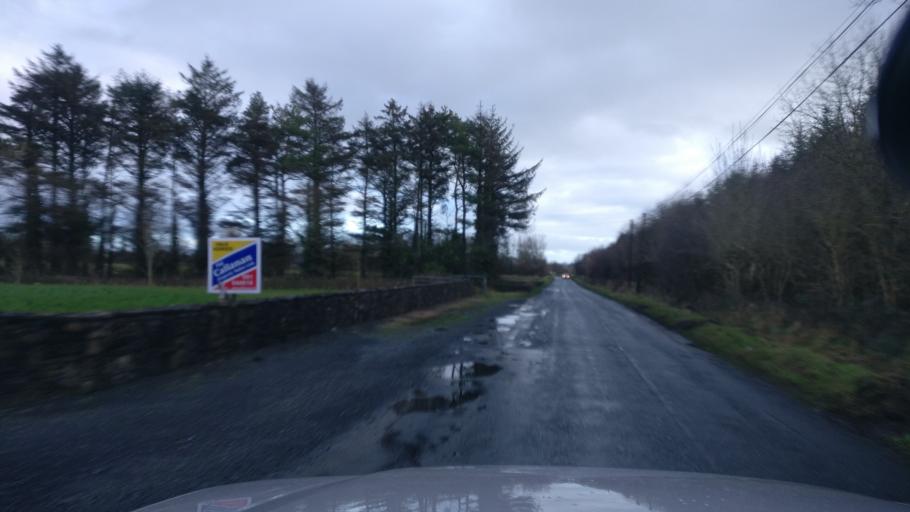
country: IE
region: Connaught
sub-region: County Galway
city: Athenry
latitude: 53.2972
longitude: -8.7037
